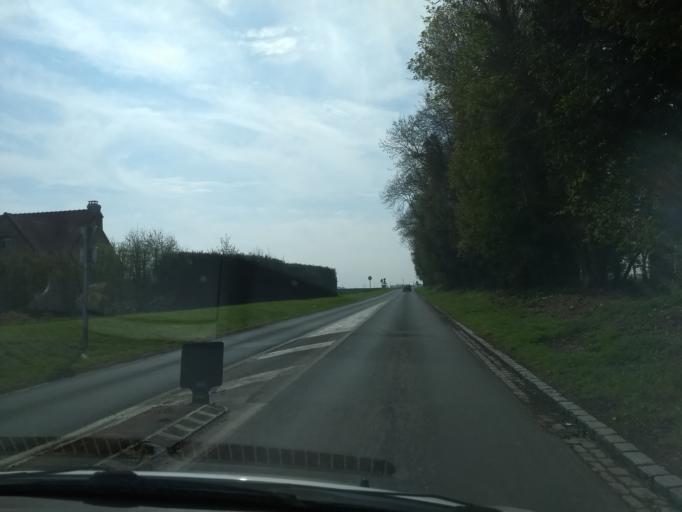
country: FR
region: Nord-Pas-de-Calais
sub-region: Departement du Nord
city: Guesnain
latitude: 50.3261
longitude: 3.1477
